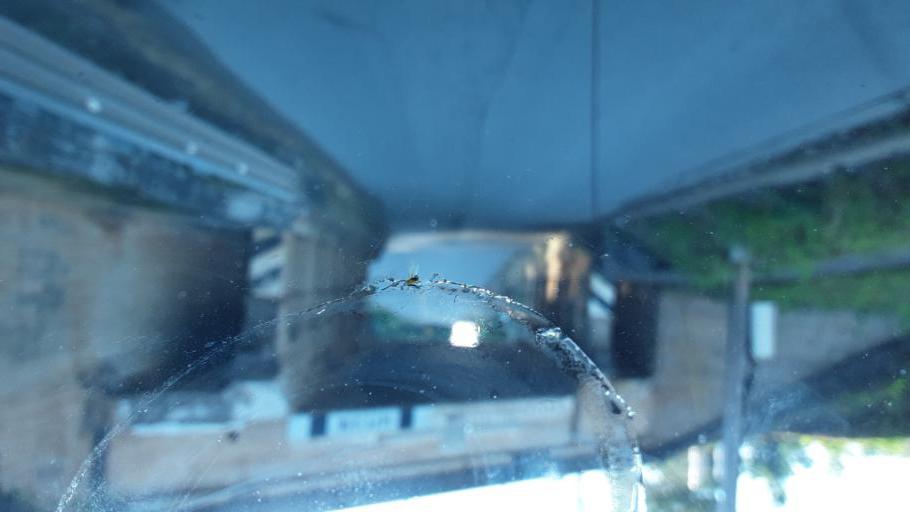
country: US
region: Virginia
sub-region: Pittsylvania County
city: Chatham
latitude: 36.8215
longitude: -79.4029
